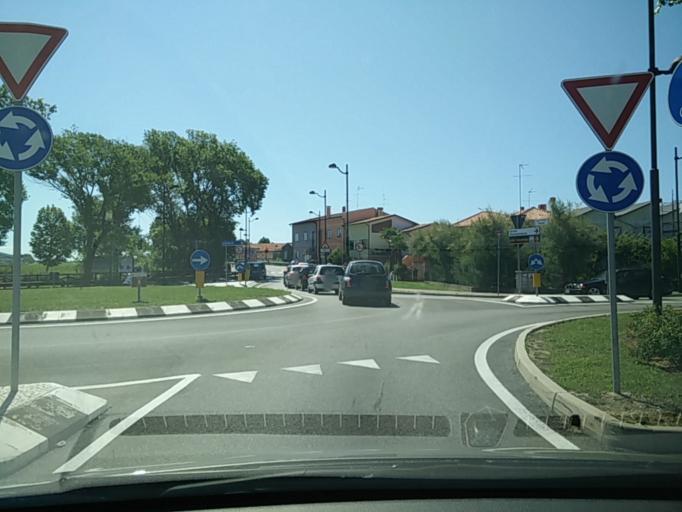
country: IT
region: Veneto
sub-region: Provincia di Venezia
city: Caorle
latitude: 45.6055
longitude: 12.8778
